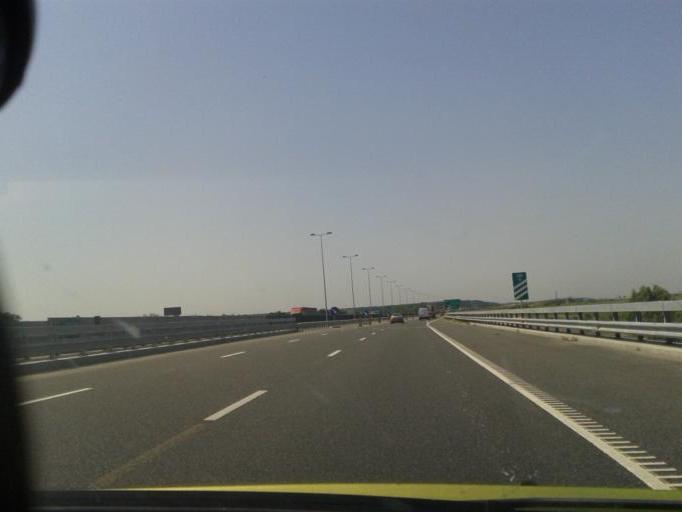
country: RO
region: Ilfov
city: Stefanestii de Jos
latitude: 44.5355
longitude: 26.1834
